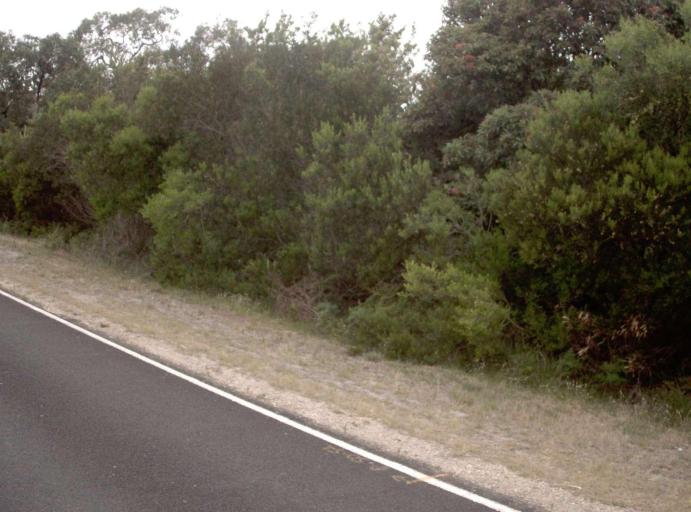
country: AU
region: Victoria
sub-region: East Gippsland
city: Bairnsdale
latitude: -38.0611
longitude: 147.5631
